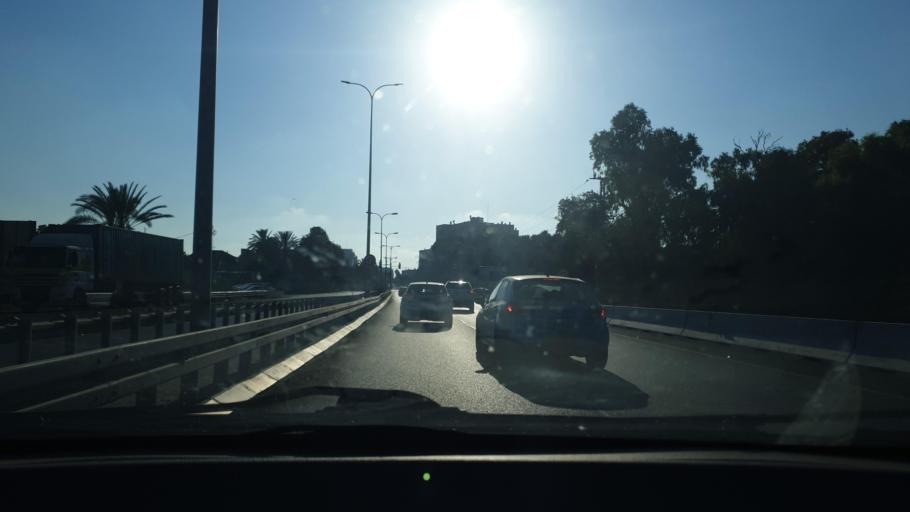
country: IL
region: Tel Aviv
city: Azor
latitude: 32.0445
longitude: 34.8150
